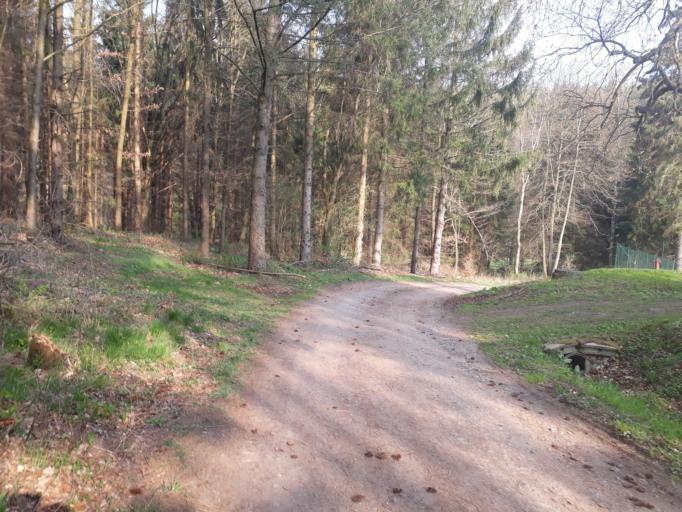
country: DE
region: Saxony
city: Reinhardtsgrimma
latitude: 50.8918
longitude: 13.7784
